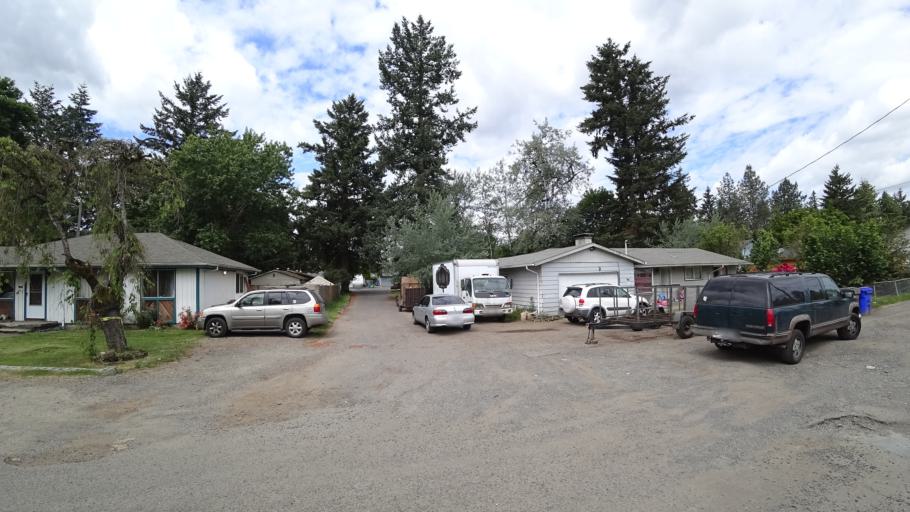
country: US
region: Oregon
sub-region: Multnomah County
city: Lents
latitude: 45.4961
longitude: -122.5275
